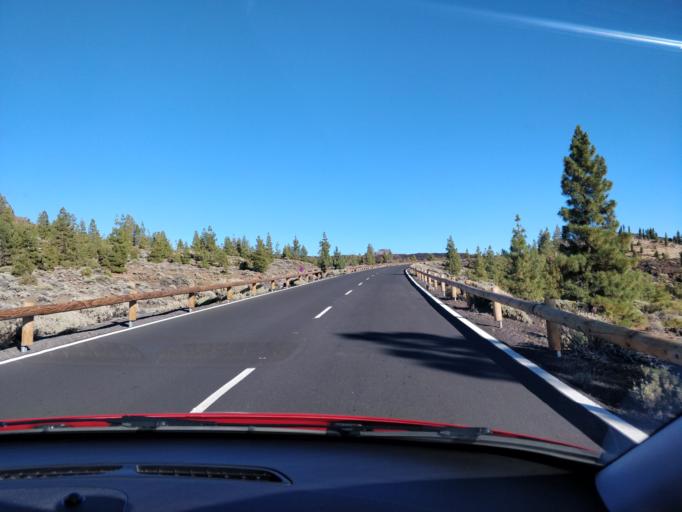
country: ES
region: Canary Islands
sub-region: Provincia de Santa Cruz de Tenerife
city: Guia de Isora
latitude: 28.2491
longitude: -16.7075
